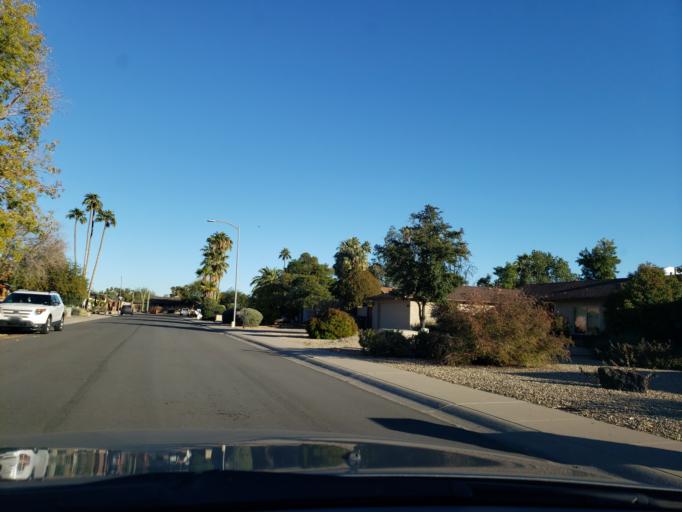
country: US
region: Arizona
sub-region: Maricopa County
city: Paradise Valley
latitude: 33.6026
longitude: -111.9744
